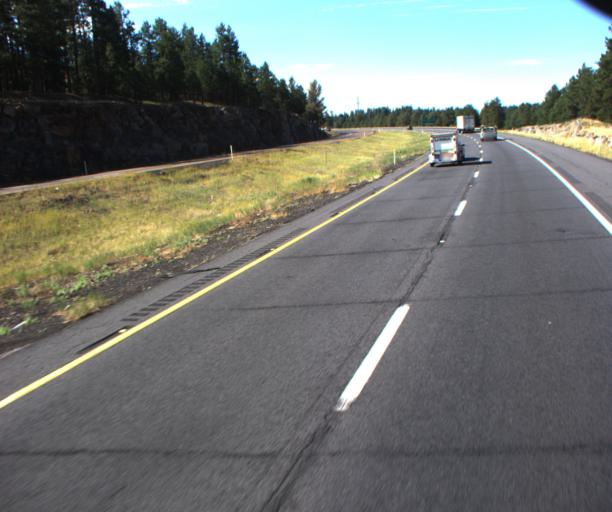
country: US
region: Arizona
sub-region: Coconino County
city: Mountainaire
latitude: 35.0649
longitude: -111.6853
